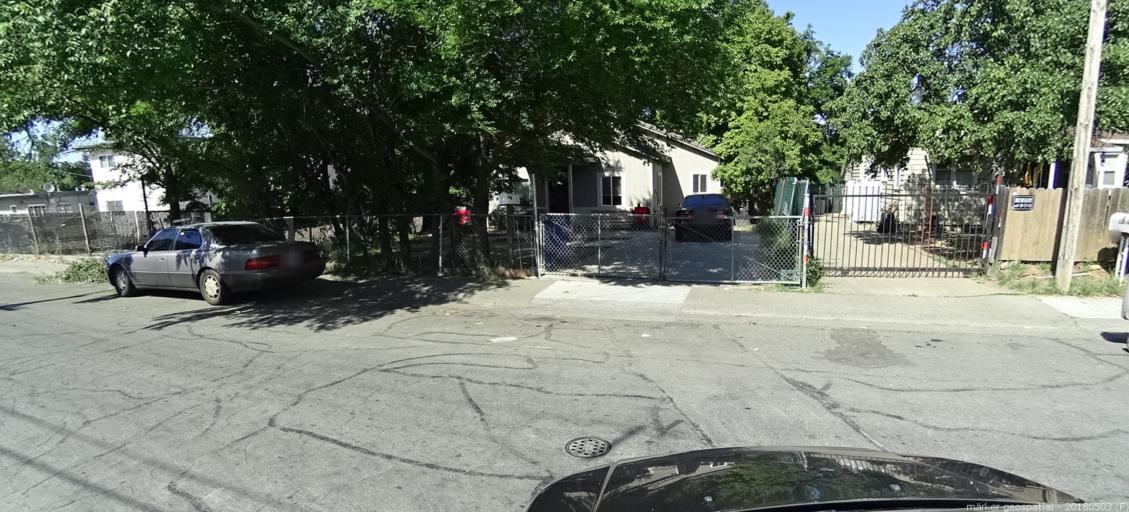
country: US
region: California
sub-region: Sacramento County
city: Arden-Arcade
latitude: 38.6208
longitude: -121.4392
